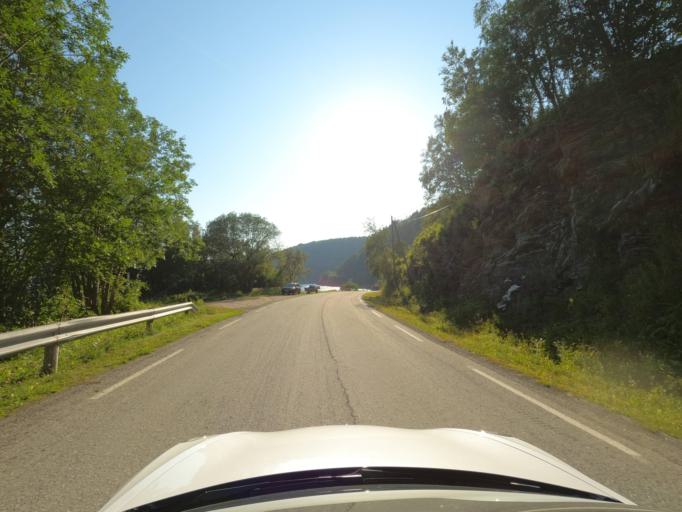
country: NO
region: Nordland
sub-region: Narvik
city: Narvik
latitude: 68.5251
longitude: 17.4423
